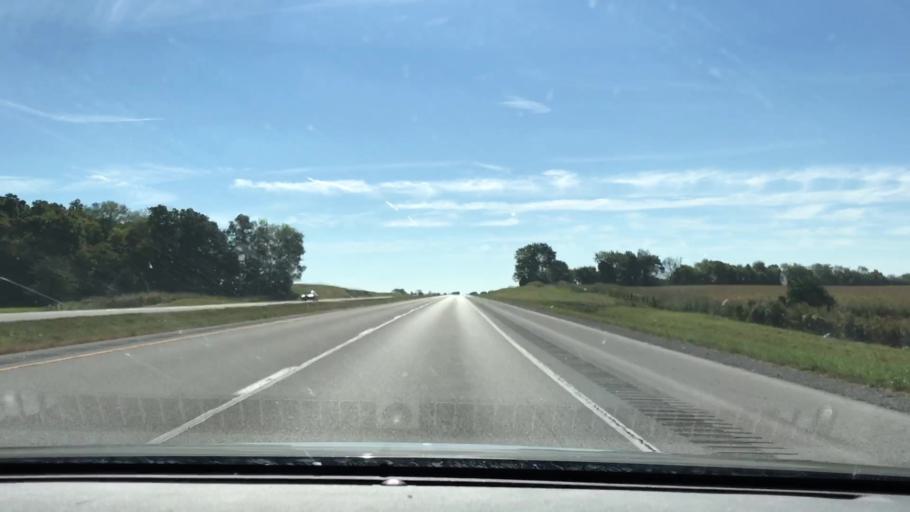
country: US
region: Kentucky
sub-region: Todd County
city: Elkton
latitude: 36.8208
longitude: -87.1450
